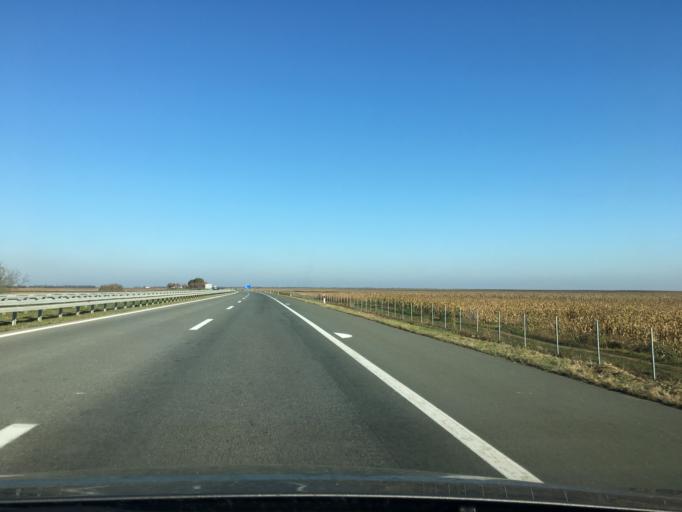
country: RS
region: Autonomna Pokrajina Vojvodina
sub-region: Severnobacki Okrug
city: Mali Igos
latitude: 45.6673
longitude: 19.7281
